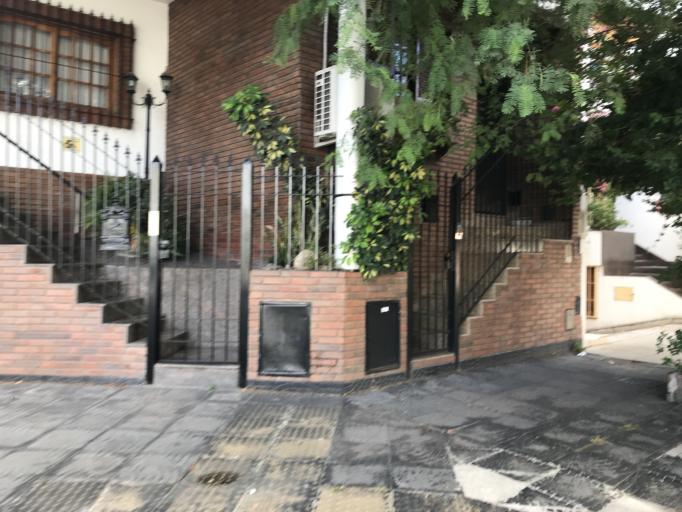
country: AR
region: Buenos Aires F.D.
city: Villa Santa Rita
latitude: -34.6319
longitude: -58.4487
